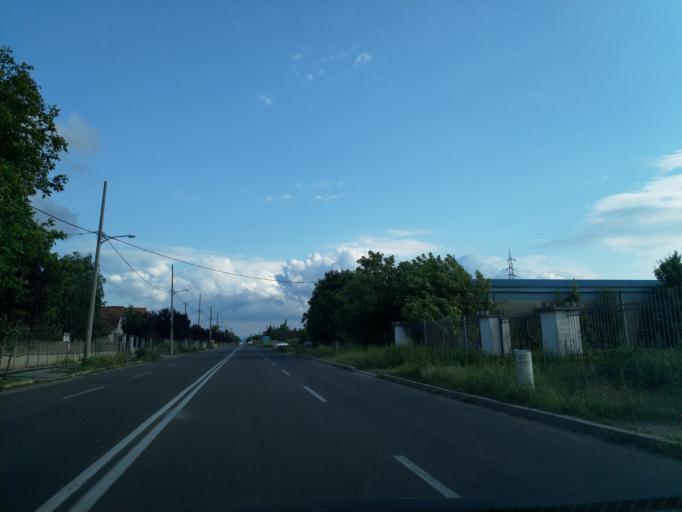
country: RS
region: Central Serbia
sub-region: Pomoravski Okrug
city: Paracin
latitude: 43.8372
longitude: 21.4157
